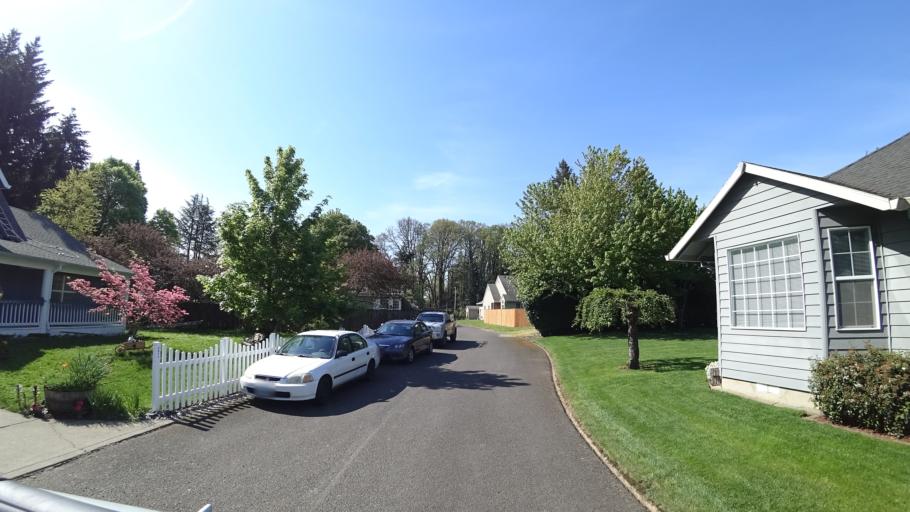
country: US
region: Oregon
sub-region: Washington County
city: Hillsboro
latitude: 45.5251
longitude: -122.9431
